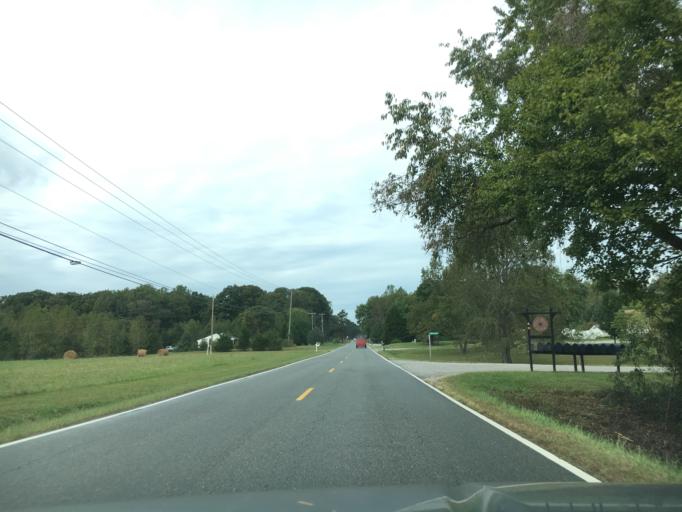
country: US
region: Virginia
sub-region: Goochland County
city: Goochland
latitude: 37.7288
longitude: -77.8344
